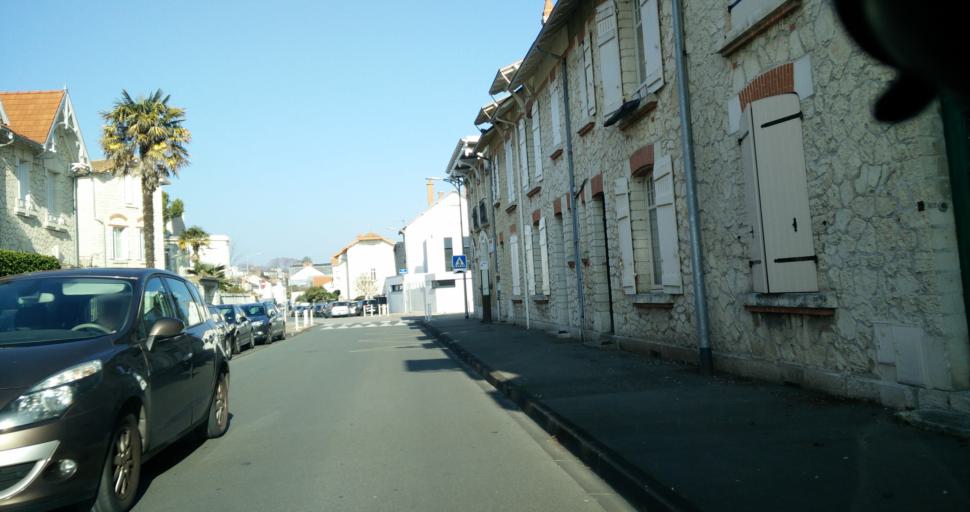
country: FR
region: Poitou-Charentes
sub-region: Departement de la Charente-Maritime
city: La Rochelle
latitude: 46.1635
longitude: -1.1585
